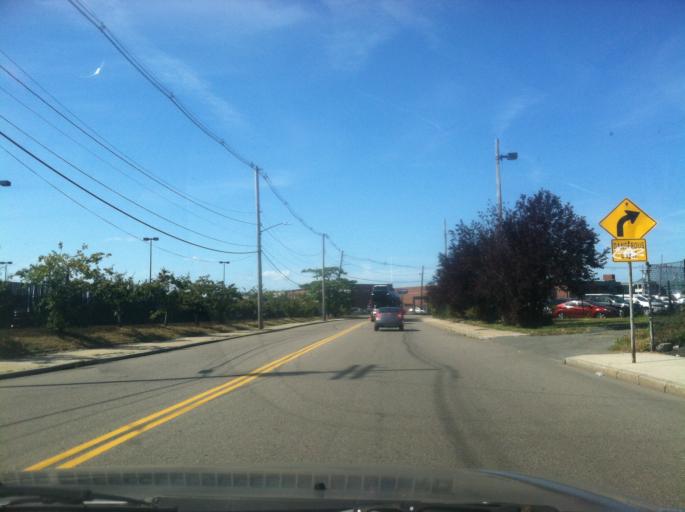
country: US
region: Massachusetts
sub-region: Suffolk County
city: Chelsea
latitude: 42.3872
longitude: -71.0185
